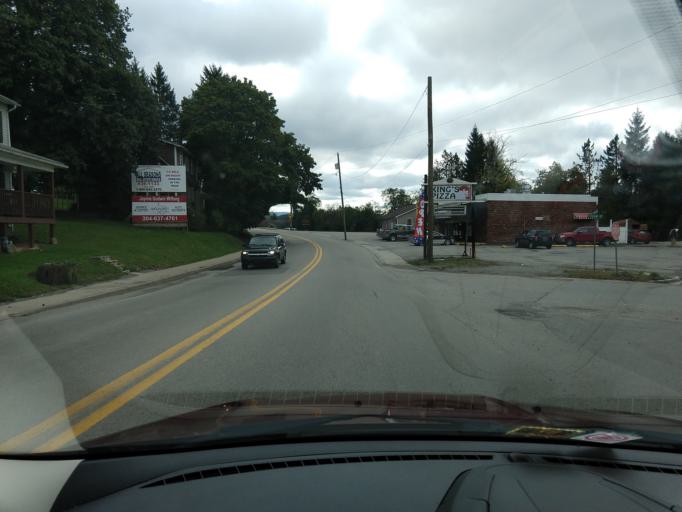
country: US
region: West Virginia
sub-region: Randolph County
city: Elkins
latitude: 38.9290
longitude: -79.8590
